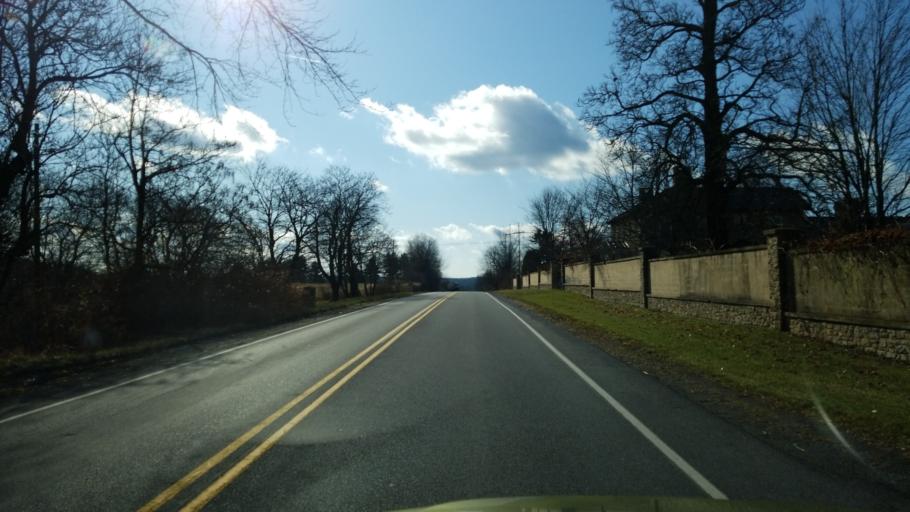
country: US
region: Pennsylvania
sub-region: Clearfield County
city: Hyde
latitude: 40.9938
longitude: -78.4420
